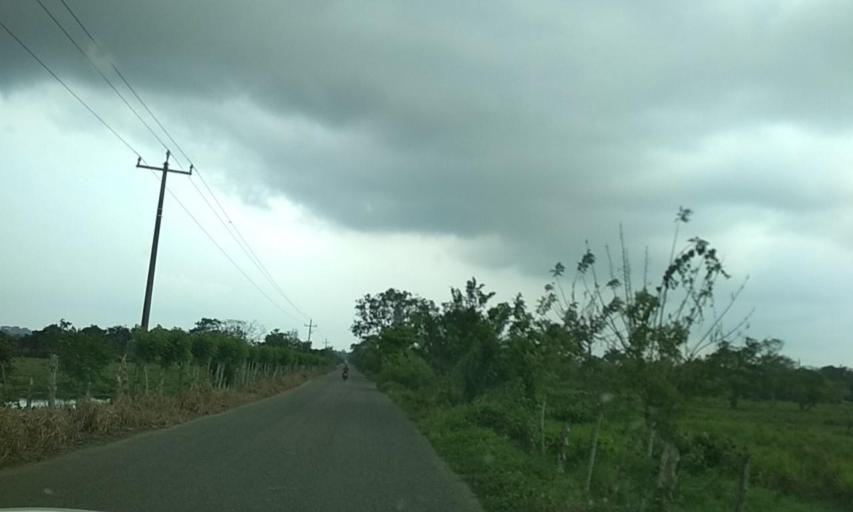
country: MX
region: Tabasco
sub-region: Huimanguillo
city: Francisco Rueda
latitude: 17.5525
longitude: -94.1237
